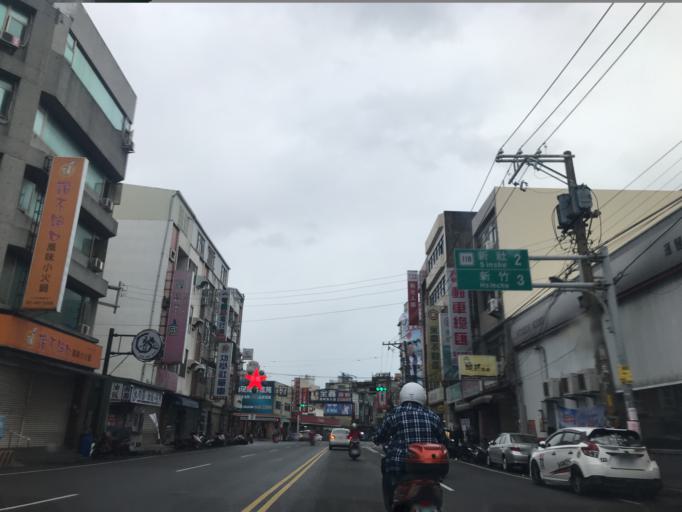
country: TW
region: Taiwan
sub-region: Hsinchu
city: Zhubei
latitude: 24.8355
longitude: 121.0194
